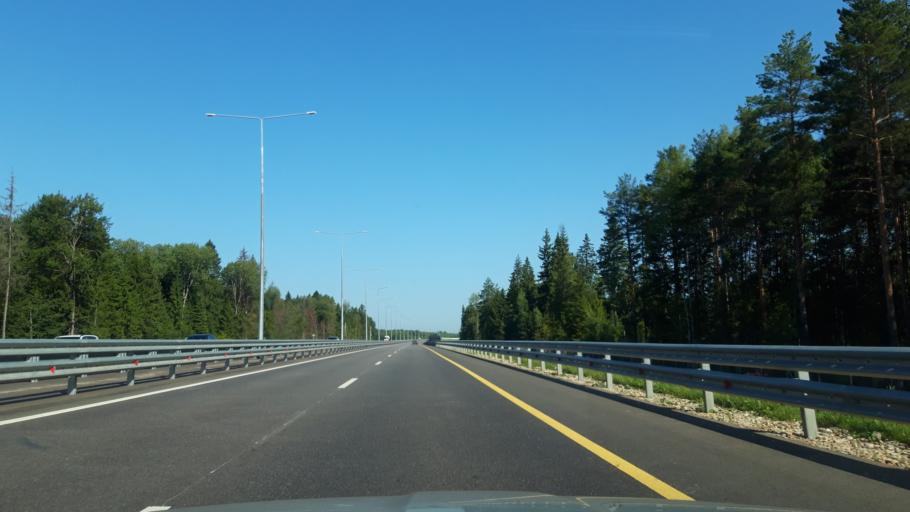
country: RU
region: Tverskaya
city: Zavidovo
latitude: 56.5085
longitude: 36.5141
